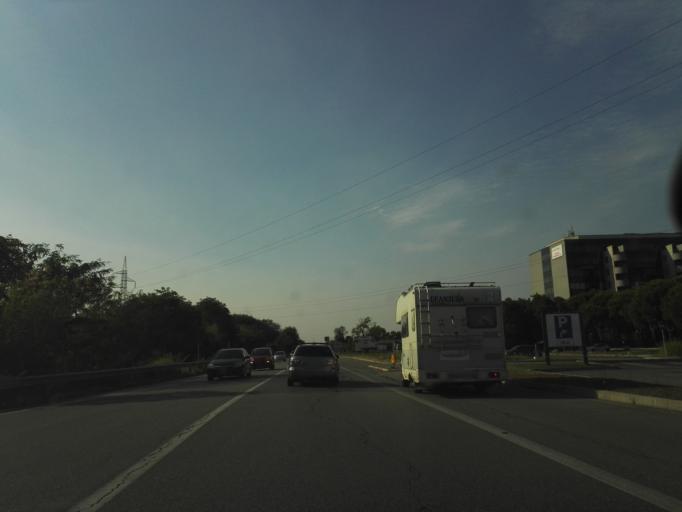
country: IT
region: Lombardy
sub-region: Citta metropolitana di Milano
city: San Giuliano Milanese
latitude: 45.3817
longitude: 9.2998
